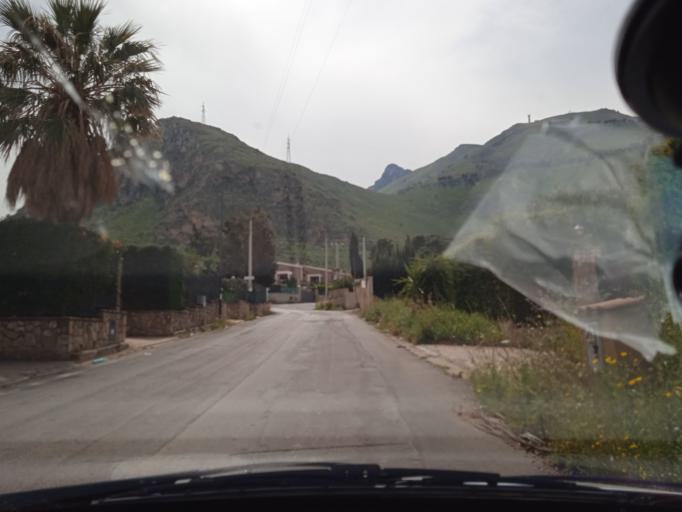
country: IT
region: Sicily
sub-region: Palermo
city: Torre Colonna-Sperone
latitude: 38.0249
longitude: 13.5761
